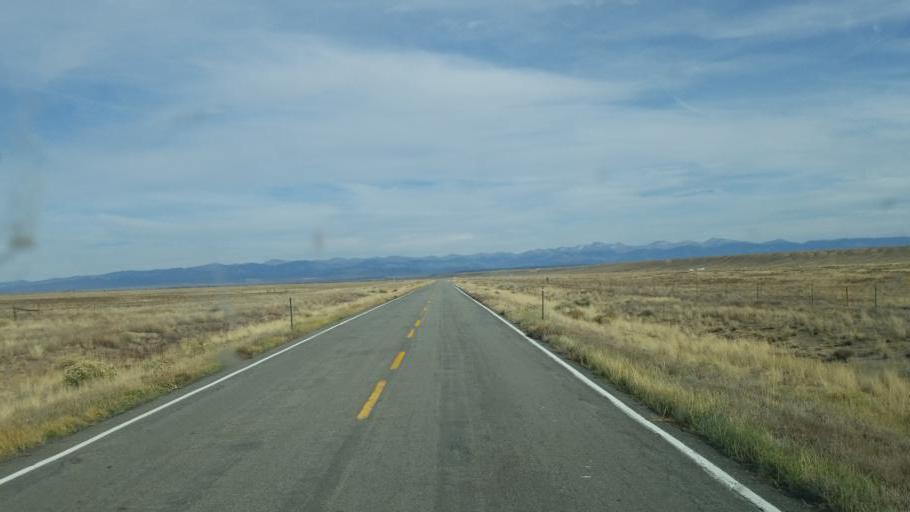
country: US
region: Colorado
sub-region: Costilla County
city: San Luis
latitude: 37.1805
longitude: -105.6290
